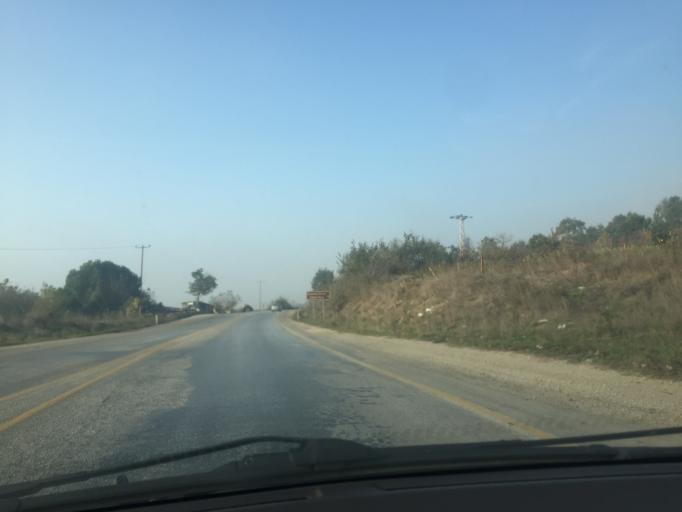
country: TR
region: Canakkale
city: Can
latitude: 40.0056
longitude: 27.0482
